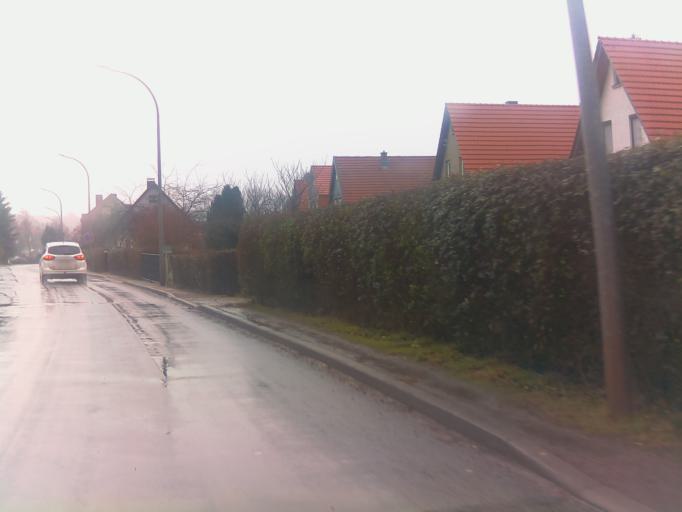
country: DE
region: Thuringia
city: Grafenroda
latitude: 50.7374
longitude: 10.7966
